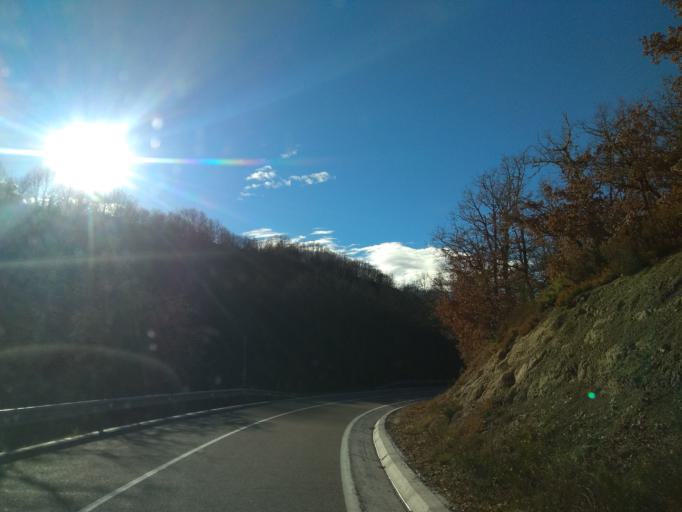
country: ES
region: Cantabria
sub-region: Provincia de Cantabria
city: San Martin de Elines
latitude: 42.9032
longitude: -3.8842
